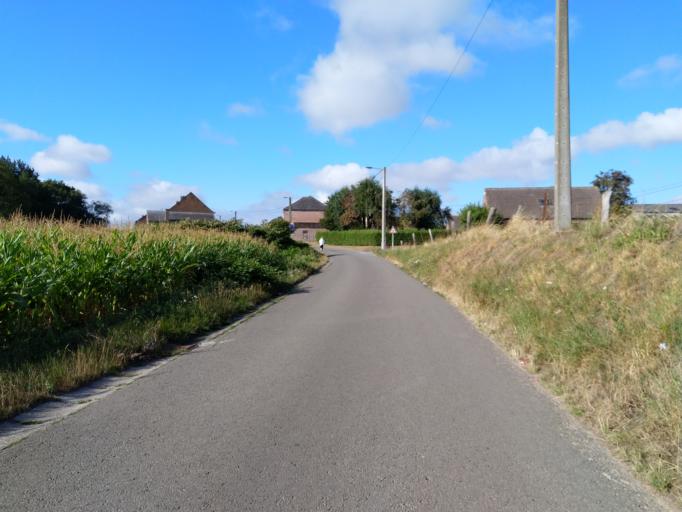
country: BE
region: Wallonia
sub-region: Province du Hainaut
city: Estinnes-au-Val
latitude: 50.3914
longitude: 4.0899
